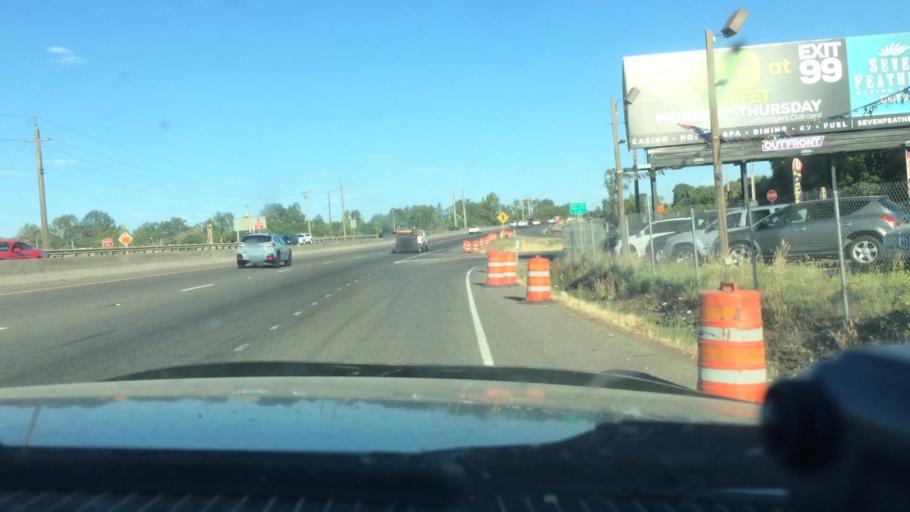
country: US
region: Oregon
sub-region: Lane County
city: Eugene
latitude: 44.0972
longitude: -123.1112
